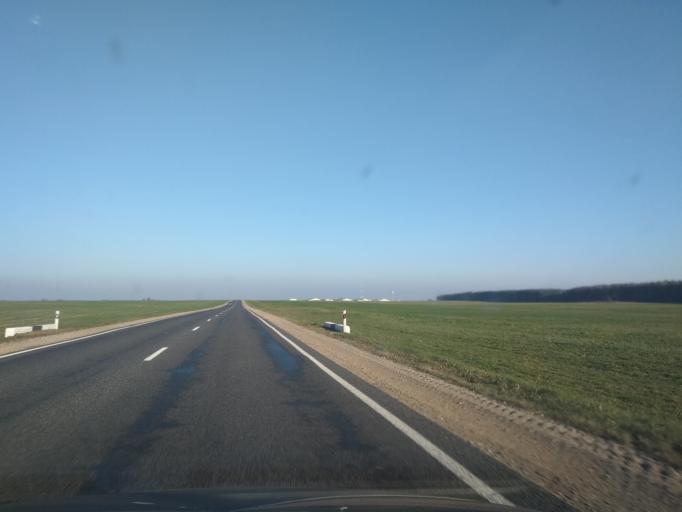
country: BY
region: Grodnenskaya
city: Svislach
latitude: 53.1295
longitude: 24.1573
